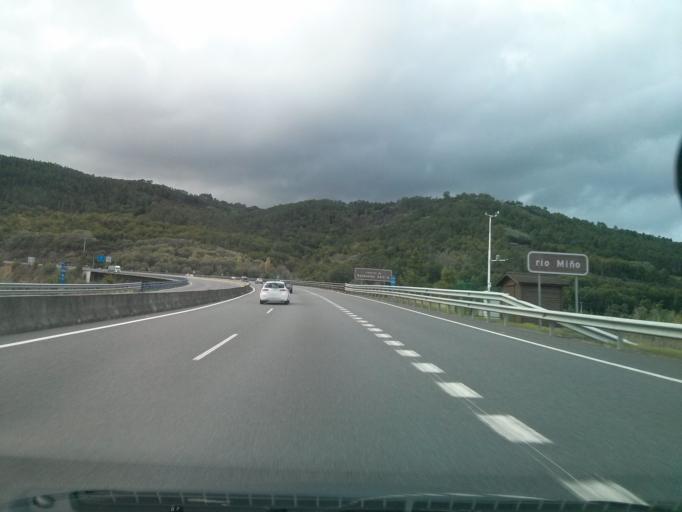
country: ES
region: Galicia
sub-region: Provincia de Ourense
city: Punxin
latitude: 42.3427
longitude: -8.0033
